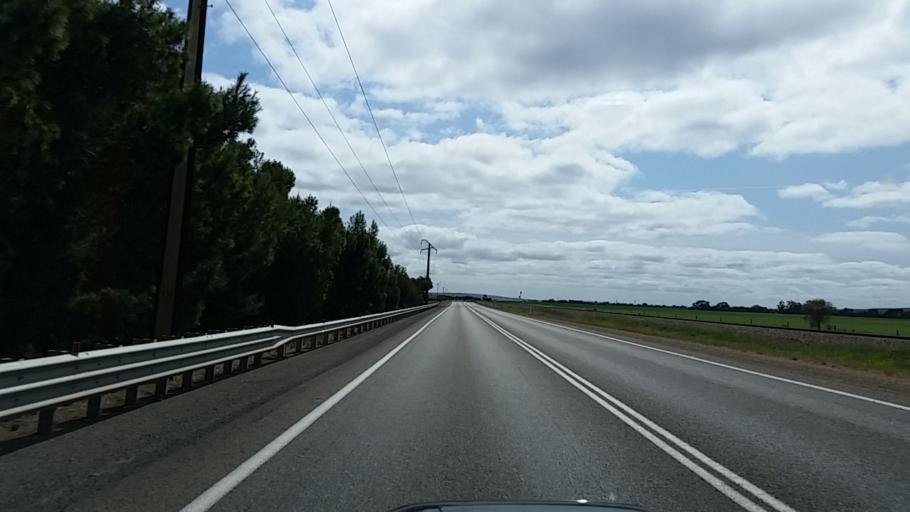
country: AU
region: South Australia
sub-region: Port Pirie City and Dists
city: Crystal Brook
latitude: -33.5338
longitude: 138.2117
